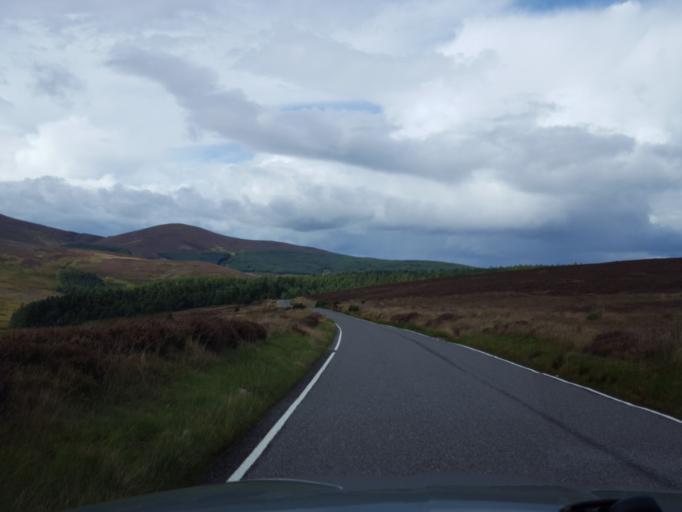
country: GB
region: Scotland
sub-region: Aberdeenshire
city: Banchory
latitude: 56.9425
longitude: -2.5755
